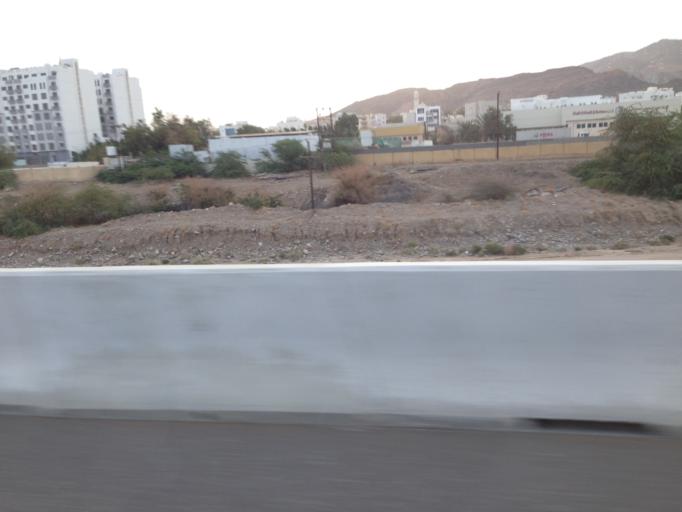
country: OM
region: Muhafazat Masqat
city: Bawshar
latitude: 23.5871
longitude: 58.4439
